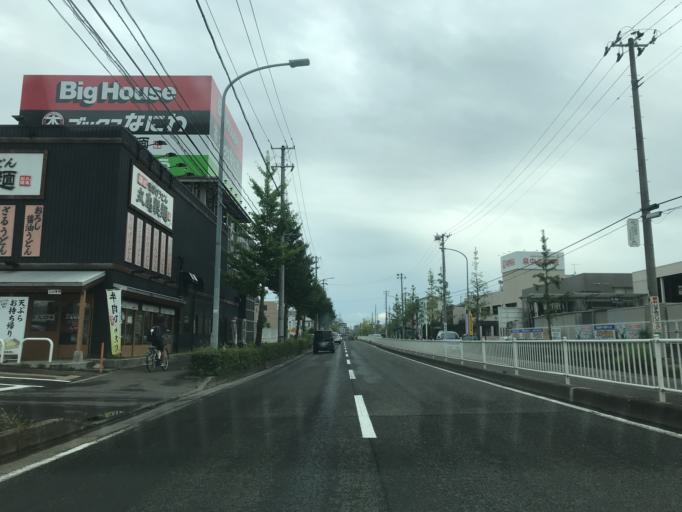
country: JP
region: Miyagi
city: Sendai-shi
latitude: 38.3159
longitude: 140.8741
